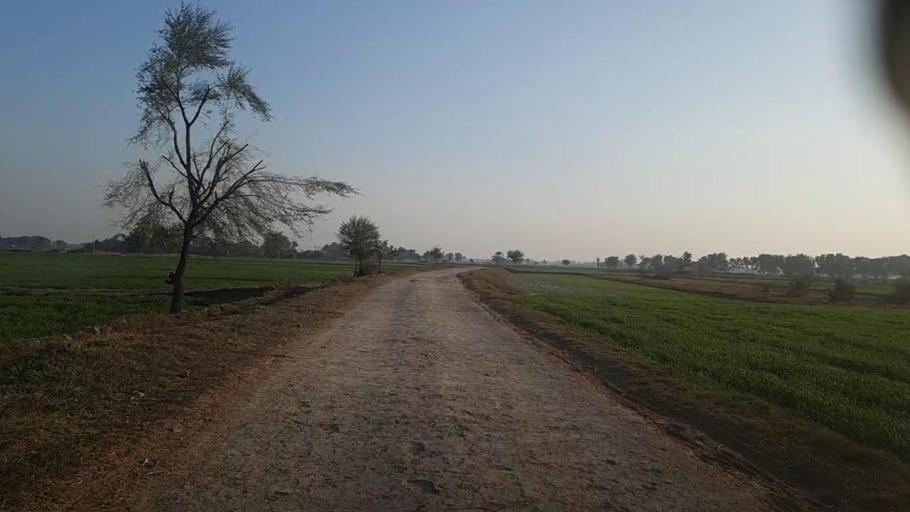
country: PK
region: Sindh
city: Khairpur
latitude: 28.0718
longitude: 69.7498
